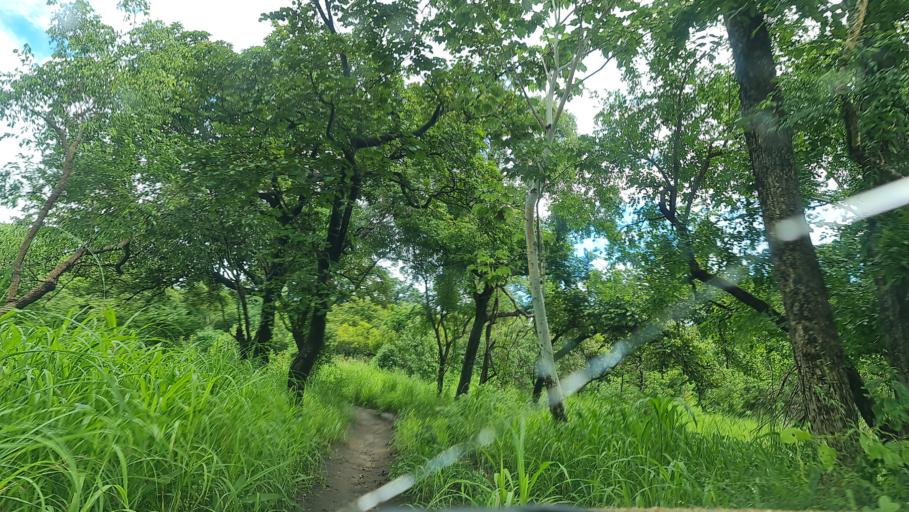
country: MW
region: Southern Region
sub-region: Nsanje District
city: Nsanje
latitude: -17.4485
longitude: 35.8399
